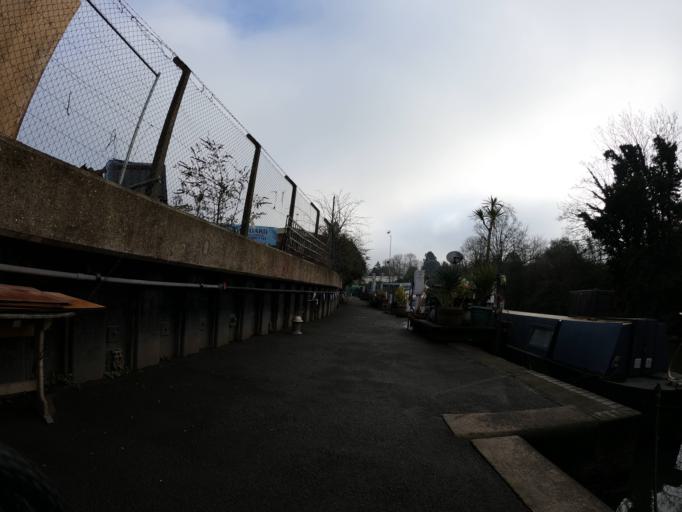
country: GB
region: England
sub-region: Greater London
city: Brentford
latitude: 51.4813
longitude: -0.3119
